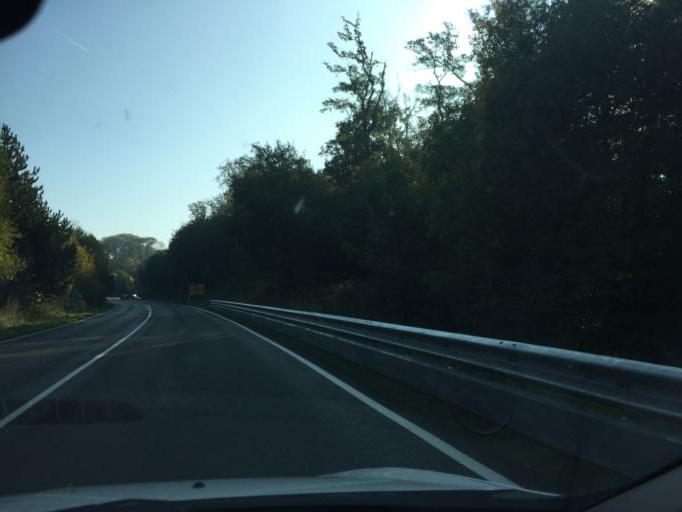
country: LU
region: Luxembourg
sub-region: Canton de Luxembourg
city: Sandweiler
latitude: 49.6089
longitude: 6.2261
